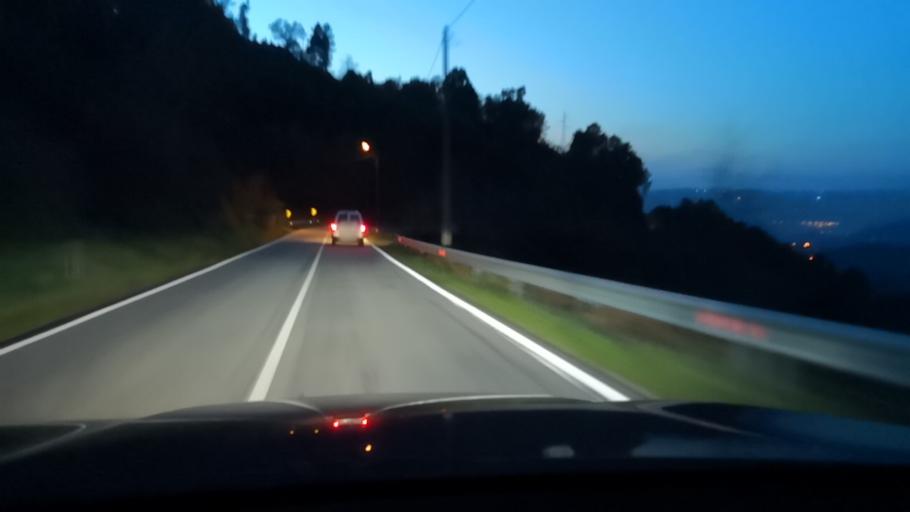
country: PT
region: Porto
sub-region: Baiao
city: Baiao
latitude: 41.2299
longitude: -8.0109
